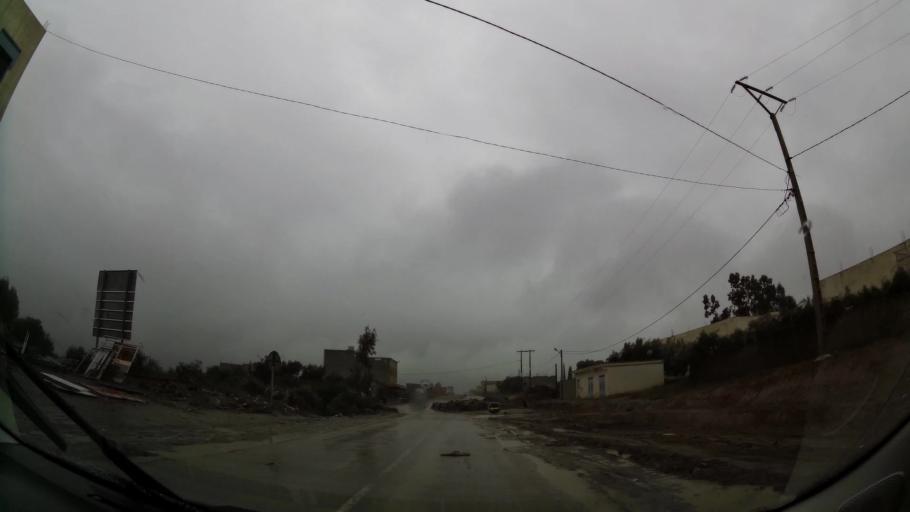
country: MA
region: Oriental
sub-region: Nador
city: Midar
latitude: 34.8766
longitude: -3.7260
